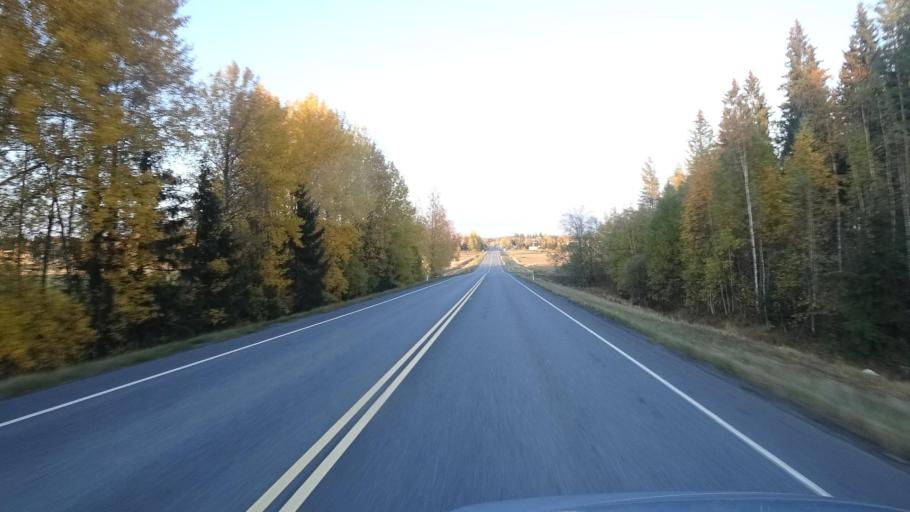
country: FI
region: Haeme
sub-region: Forssa
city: Jokioinen
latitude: 60.7997
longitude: 23.5147
